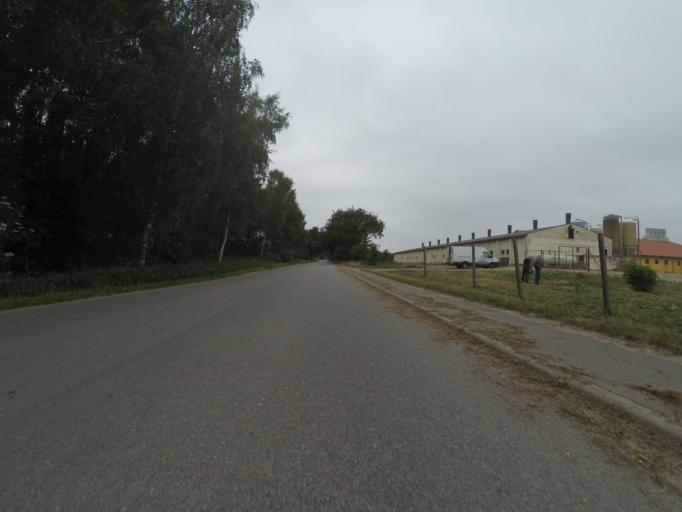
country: DE
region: Mecklenburg-Vorpommern
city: Goldberg
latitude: 53.5452
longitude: 12.0484
